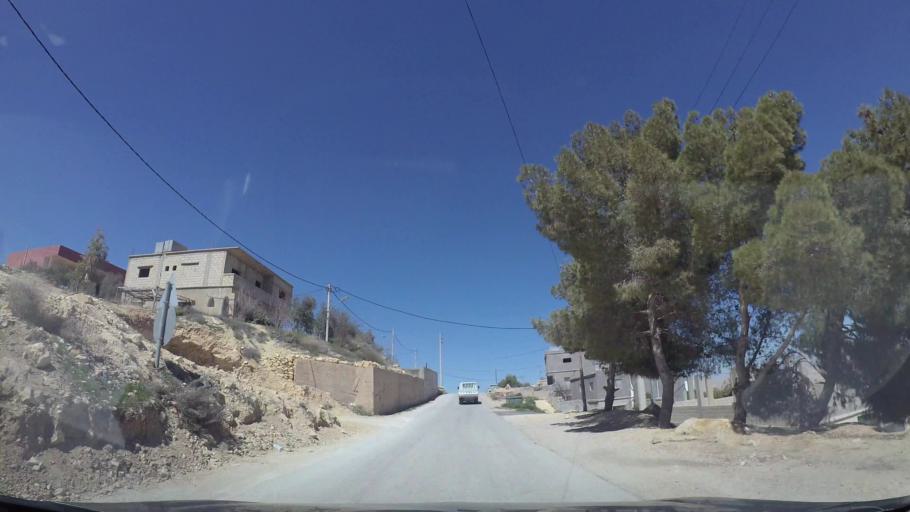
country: JO
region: Tafielah
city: At Tafilah
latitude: 30.8380
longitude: 35.5745
